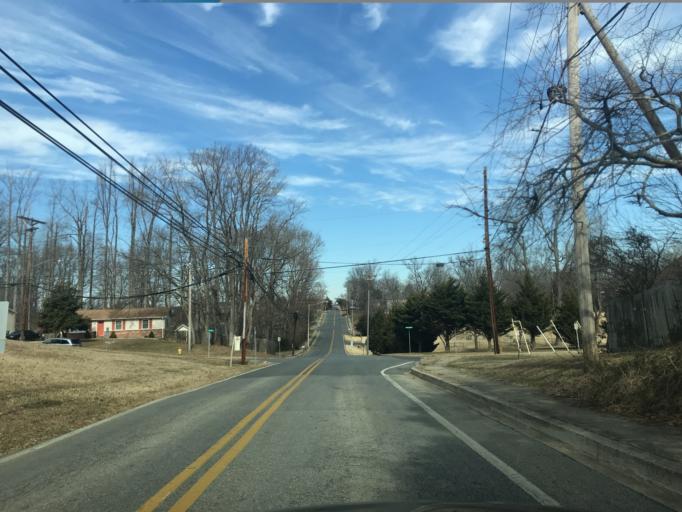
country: US
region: Maryland
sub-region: Charles County
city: La Plata
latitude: 38.5200
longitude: -76.9779
